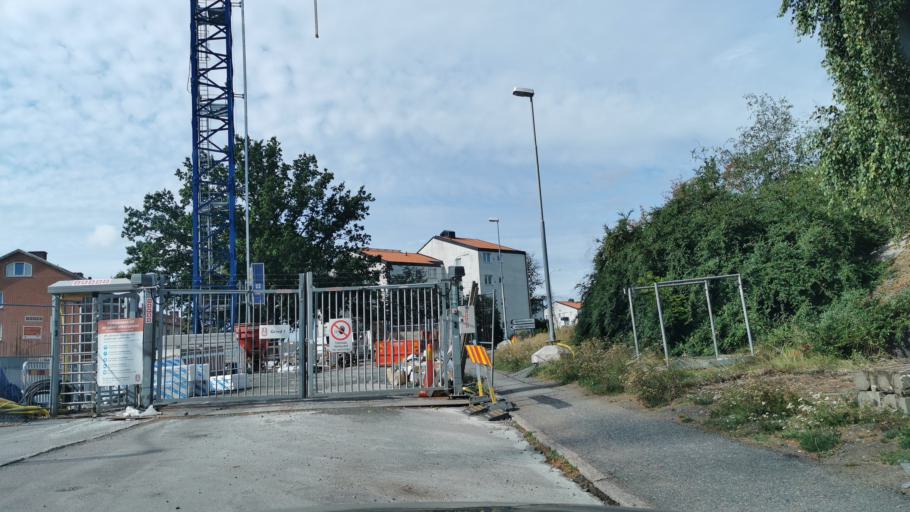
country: SE
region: Vaestra Goetaland
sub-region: Goteborg
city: Majorna
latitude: 57.6575
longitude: 11.9313
